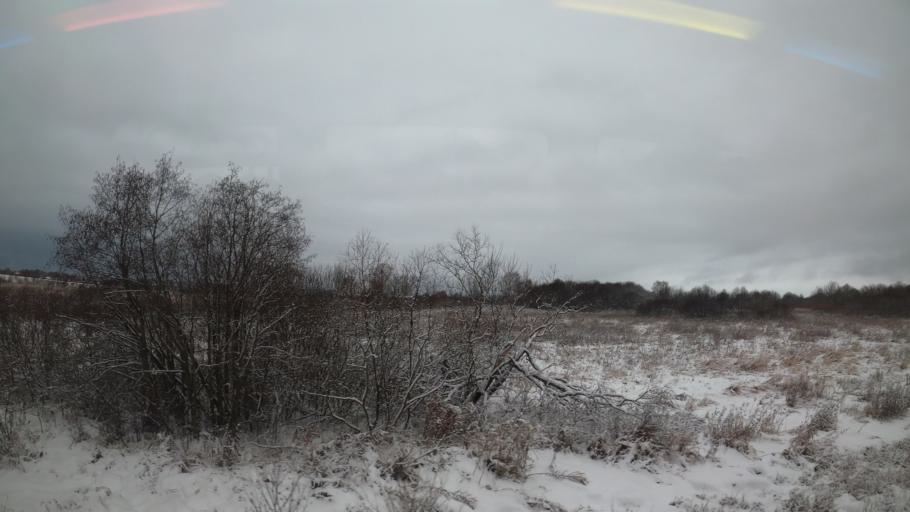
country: RU
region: Jaroslavl
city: Pereslavl'-Zalesskiy
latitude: 56.7183
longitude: 38.9083
